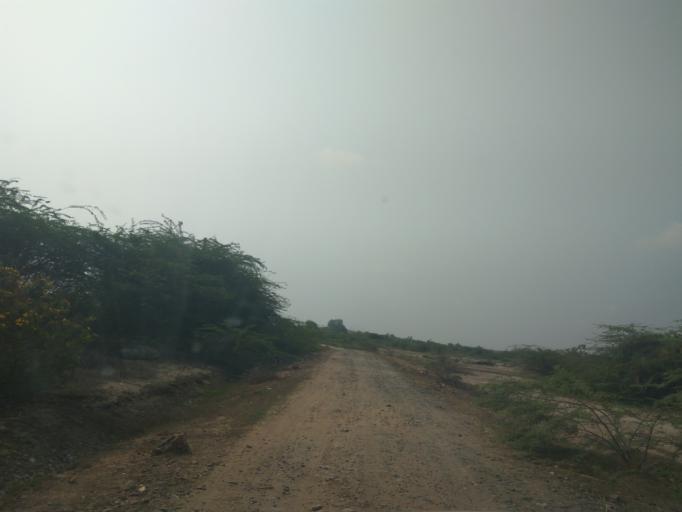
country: IN
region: Andhra Pradesh
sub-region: Prakasam
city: Kandukur
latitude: 15.0774
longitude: 79.6078
